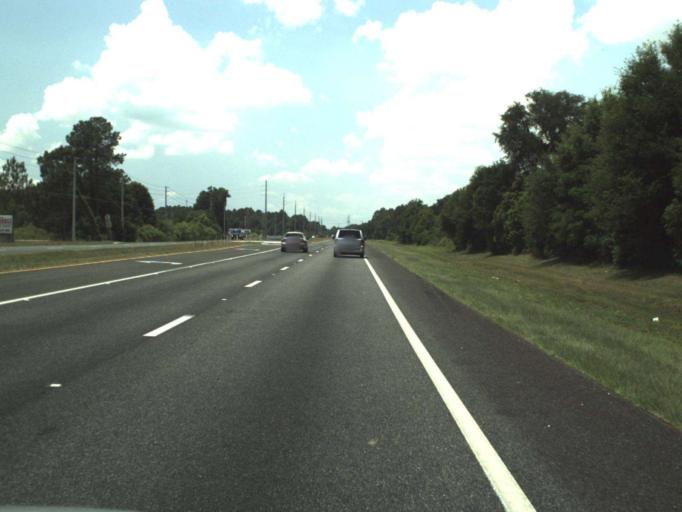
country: US
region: Florida
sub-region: Lake County
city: Fruitland Park
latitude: 28.8139
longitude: -81.9325
